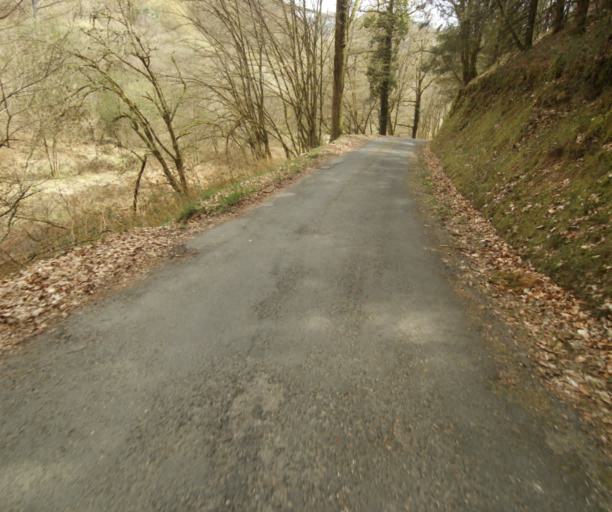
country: FR
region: Limousin
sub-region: Departement de la Correze
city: Naves
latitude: 45.3150
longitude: 1.7785
